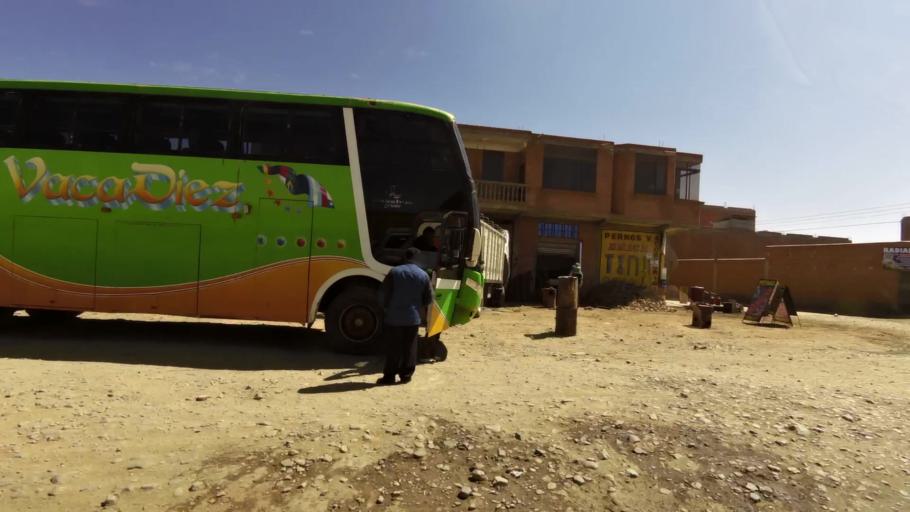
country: BO
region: La Paz
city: La Paz
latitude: -16.5517
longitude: -68.1846
